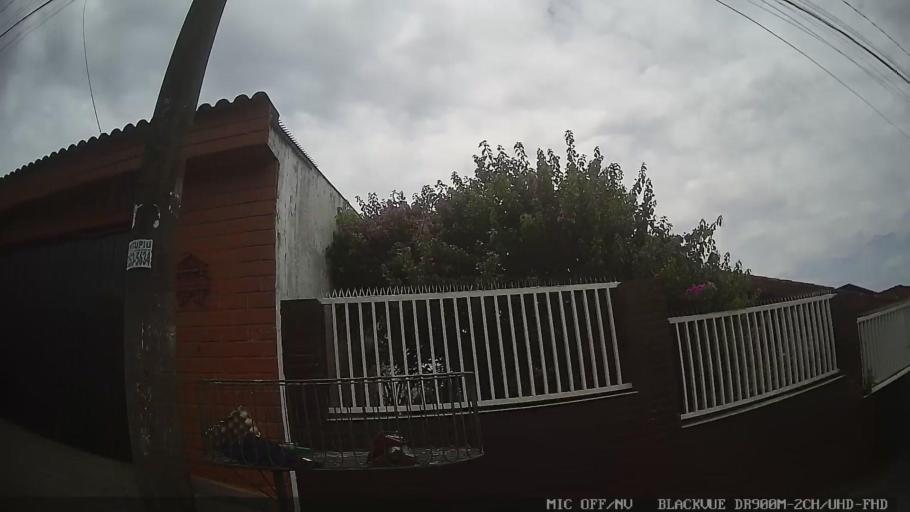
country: BR
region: Sao Paulo
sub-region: Ribeirao Pires
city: Ribeirao Pires
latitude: -23.7227
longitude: -46.4172
